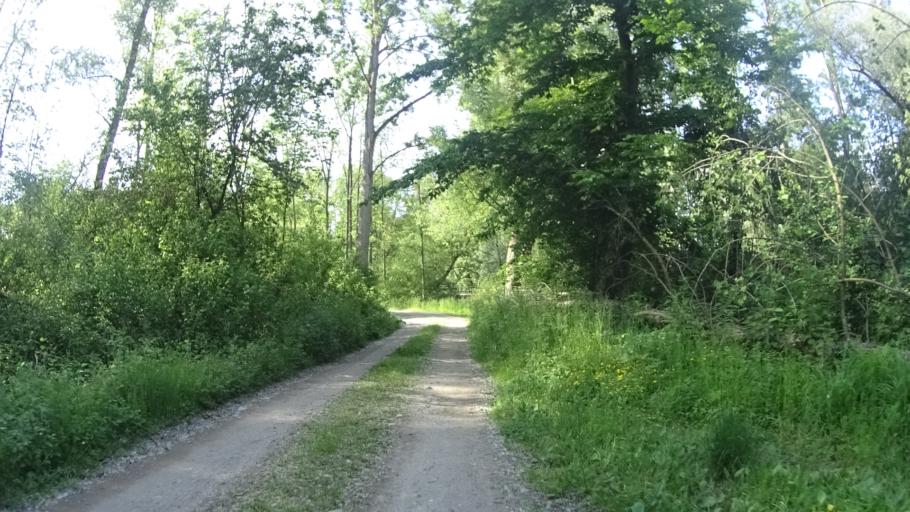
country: DE
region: Baden-Wuerttemberg
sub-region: Freiburg Region
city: Breisach am Rhein
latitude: 48.0022
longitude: 7.6190
